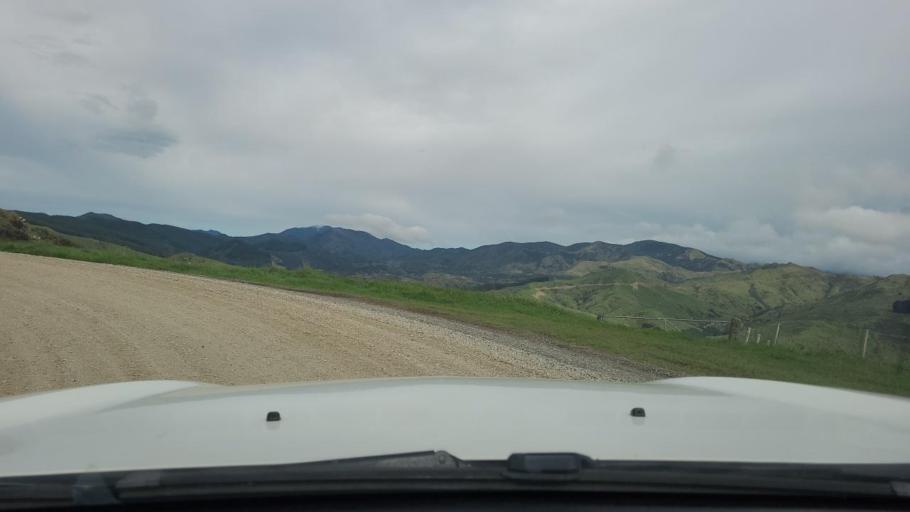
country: NZ
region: Wellington
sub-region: South Wairarapa District
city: Waipawa
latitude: -41.3785
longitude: 175.4687
